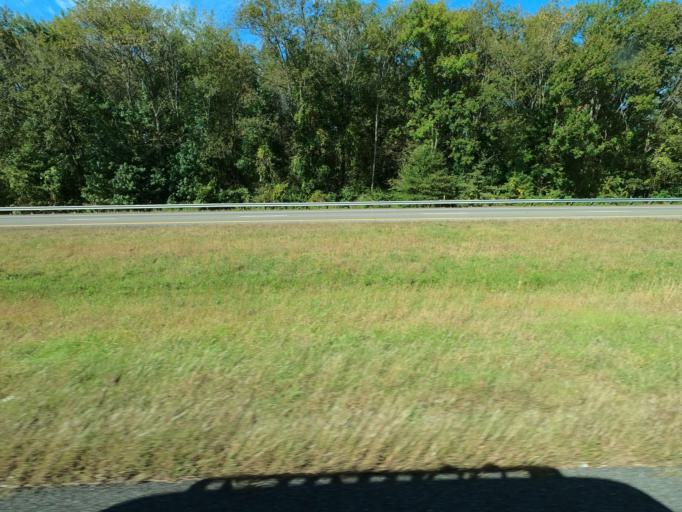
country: US
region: Tennessee
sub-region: Haywood County
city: Brownsville
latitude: 35.5086
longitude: -89.2647
